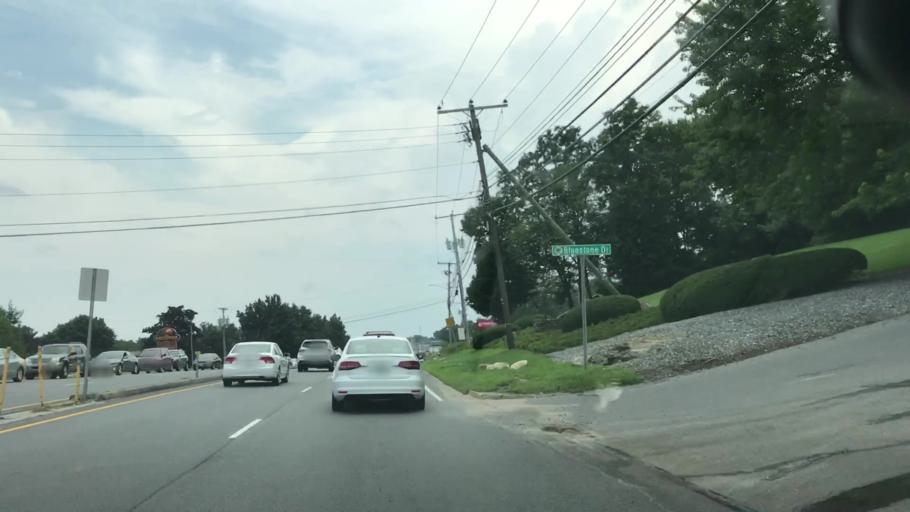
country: US
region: New Hampshire
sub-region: Hillsborough County
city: Hudson
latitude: 42.7190
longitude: -71.4426
